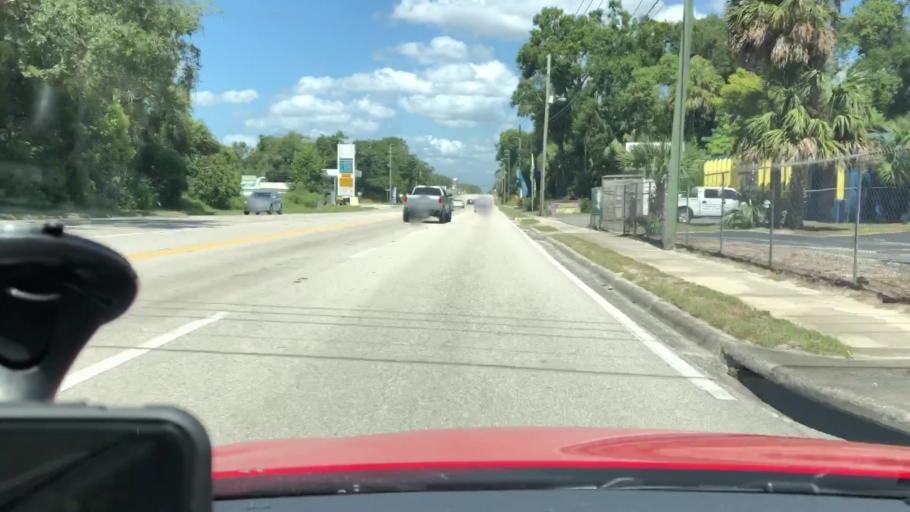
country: US
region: Florida
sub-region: Volusia County
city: West DeLand
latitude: 29.0154
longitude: -81.3238
